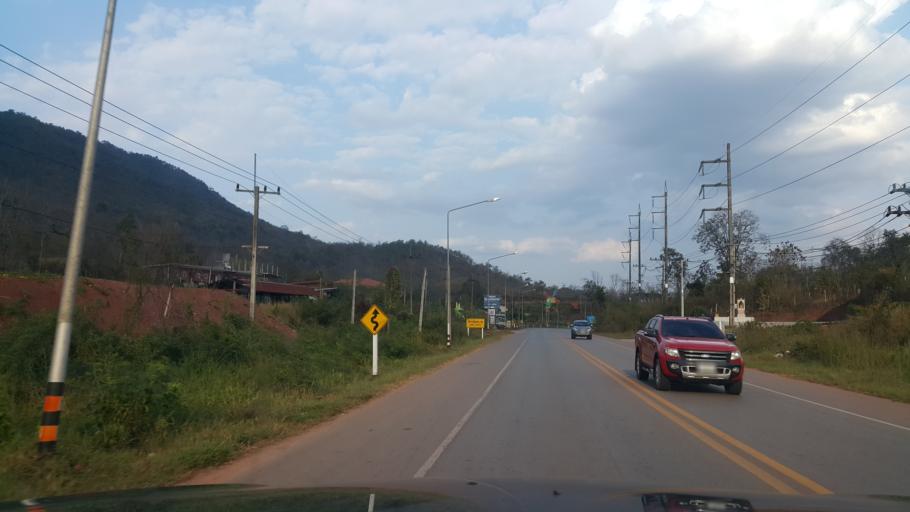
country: TH
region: Loei
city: Dan Sai
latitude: 17.2807
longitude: 101.1717
